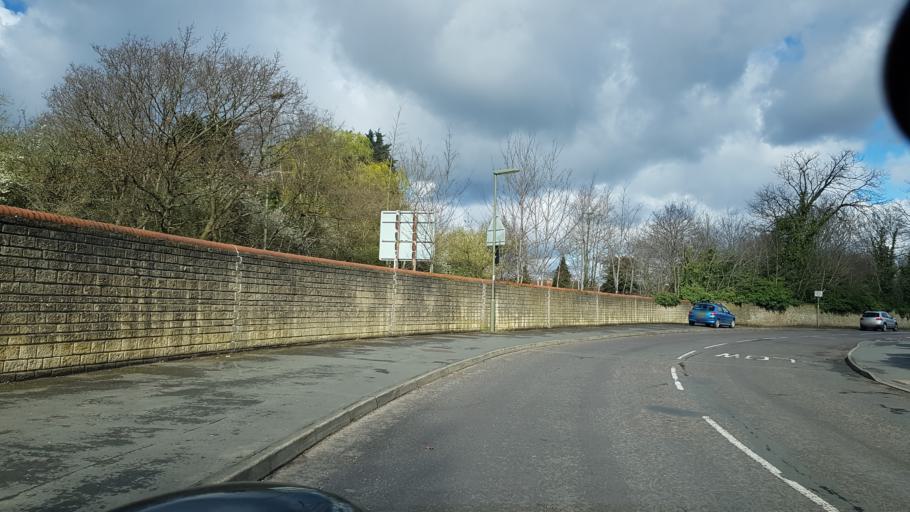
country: GB
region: England
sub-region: Surrey
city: Guildford
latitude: 51.2537
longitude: -0.5731
